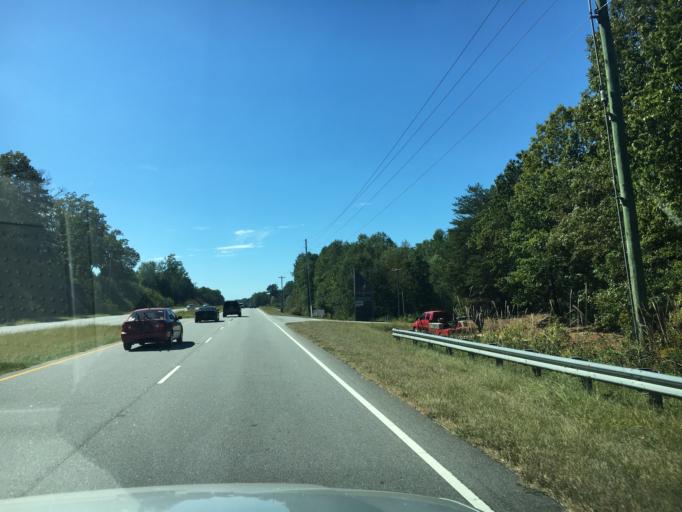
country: US
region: South Carolina
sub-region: Oconee County
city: Utica
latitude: 34.7020
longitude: -82.9160
